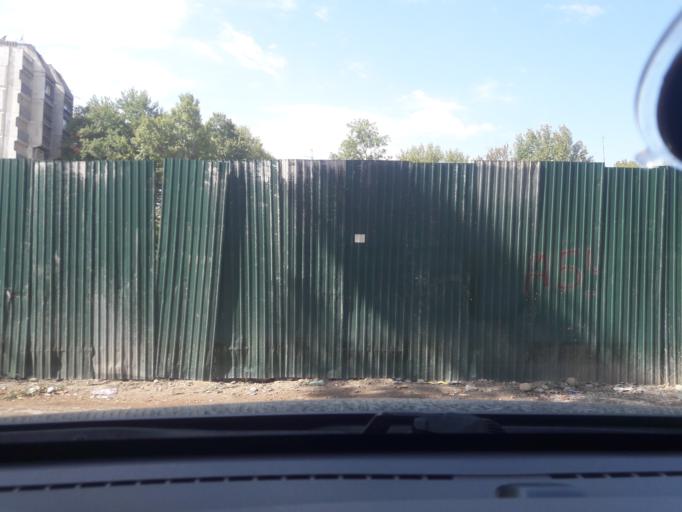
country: TJ
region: Dushanbe
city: Dushanbe
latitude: 38.5859
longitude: 68.7496
